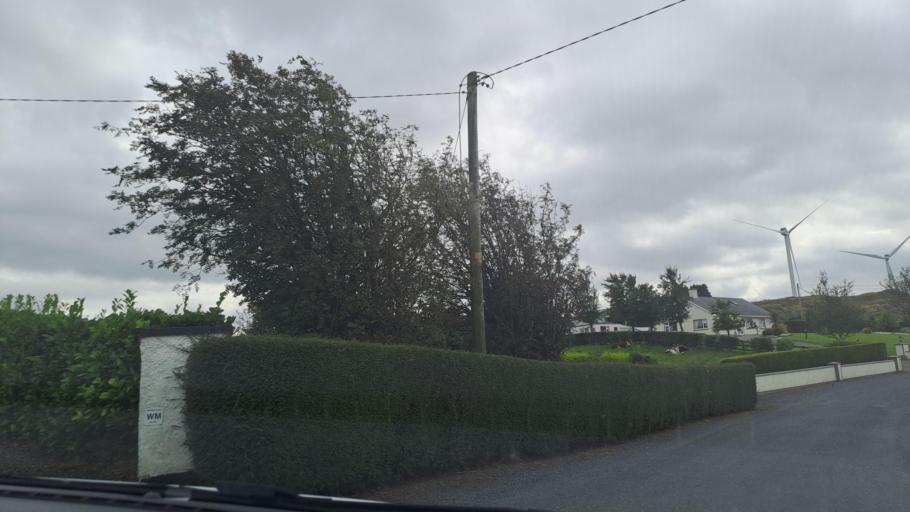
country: IE
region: Ulster
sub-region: An Cabhan
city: Kingscourt
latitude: 53.9588
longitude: -6.8793
